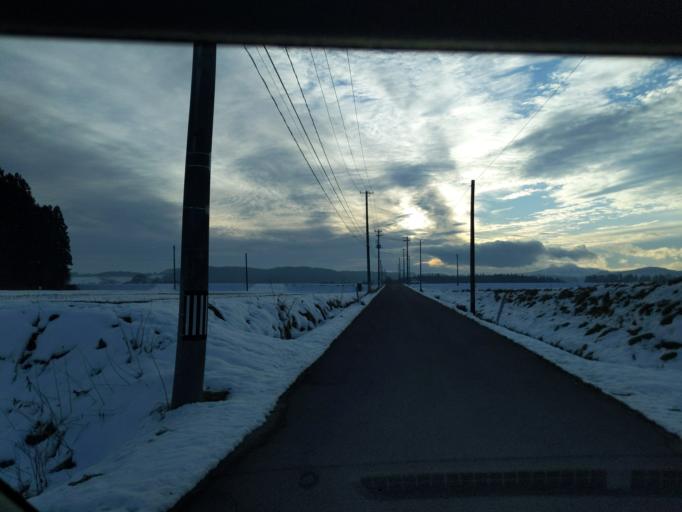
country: JP
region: Iwate
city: Mizusawa
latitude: 39.0617
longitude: 141.0913
